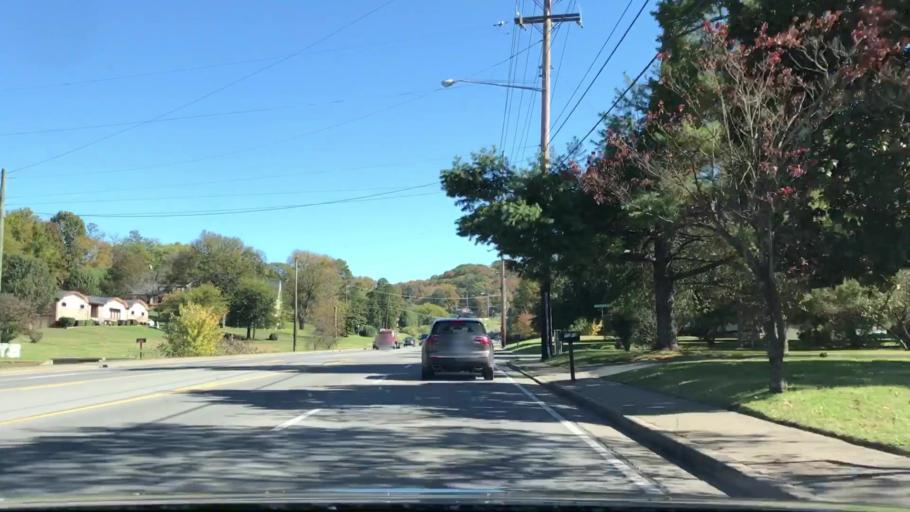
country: US
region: Tennessee
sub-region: Williamson County
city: Brentwood Estates
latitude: 36.0395
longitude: -86.7382
